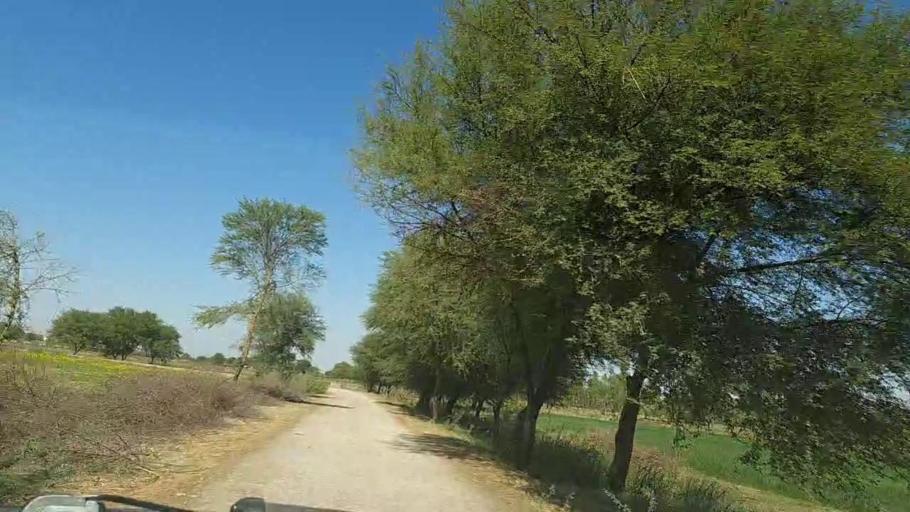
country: PK
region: Sindh
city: Dhoro Naro
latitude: 25.5265
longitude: 69.5063
